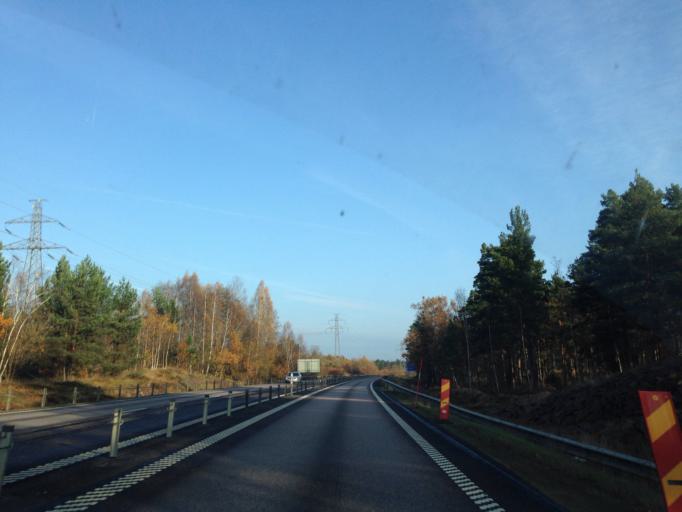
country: SE
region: Kalmar
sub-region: Oskarshamns Kommun
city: Oskarshamn
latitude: 57.2569
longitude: 16.4223
